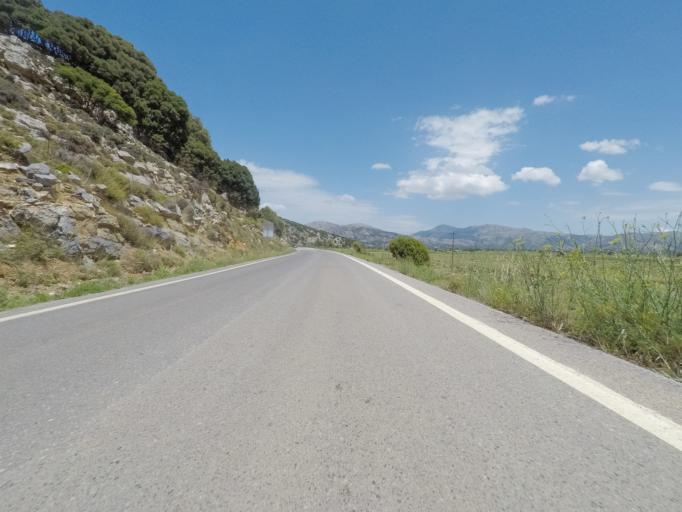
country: GR
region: Crete
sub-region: Nomos Irakleiou
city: Mokhos
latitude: 35.1946
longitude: 25.4460
